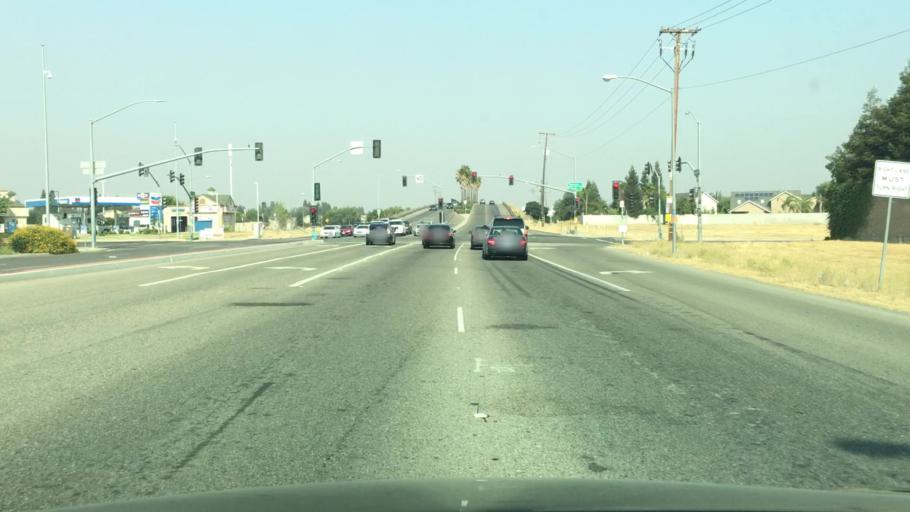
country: US
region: California
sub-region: Fresno County
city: Biola
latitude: 36.8369
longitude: -119.8904
